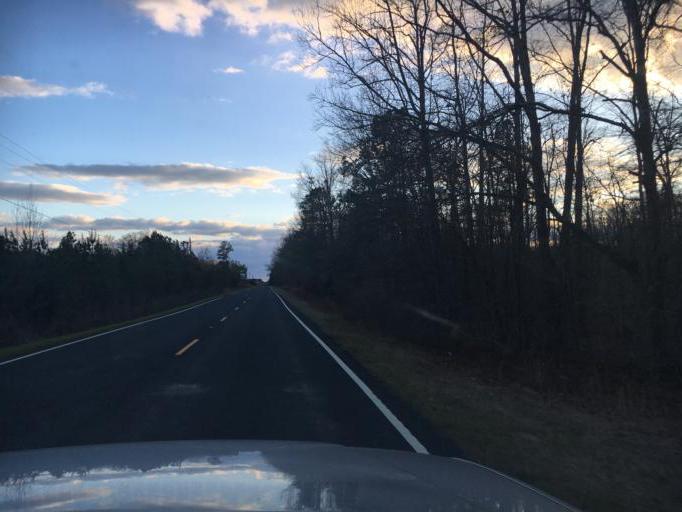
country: US
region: South Carolina
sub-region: Greenwood County
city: Greenwood
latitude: 34.0695
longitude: -82.2259
